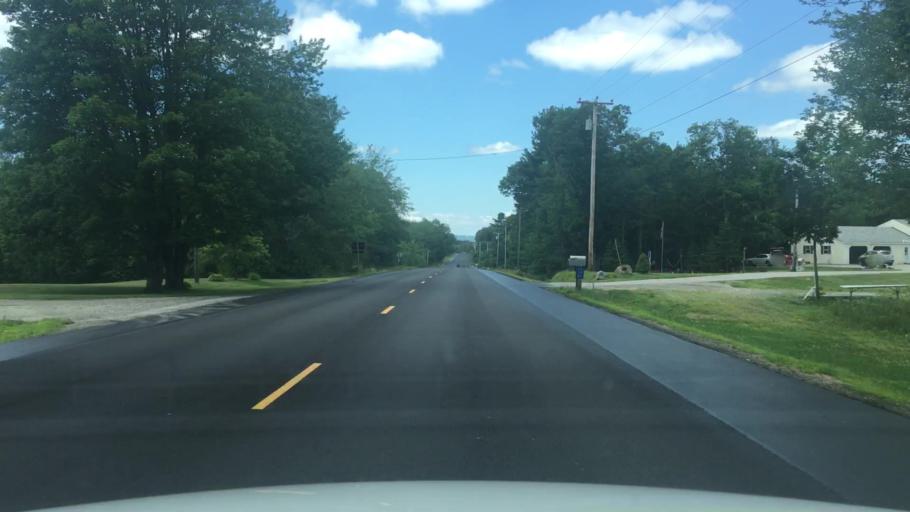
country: US
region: Maine
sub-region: Waldo County
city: Searsmont
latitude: 44.3982
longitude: -69.1444
